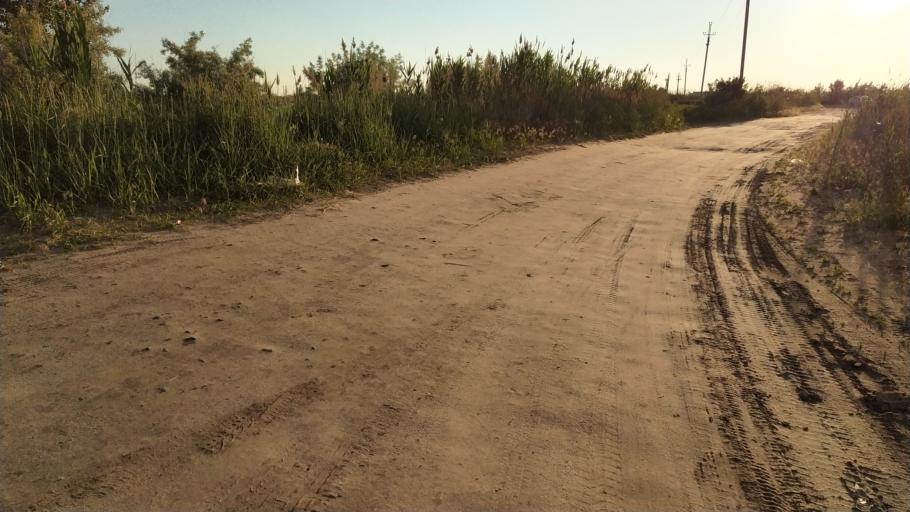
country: RU
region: Rostov
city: Bataysk
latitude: 47.1418
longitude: 39.6641
